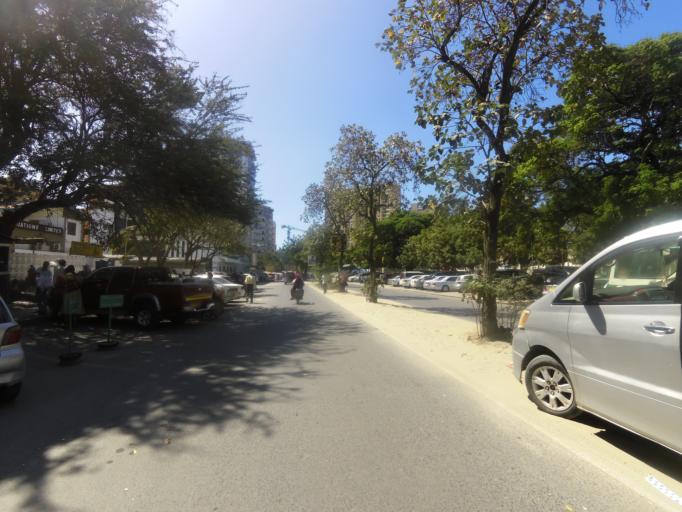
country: TZ
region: Dar es Salaam
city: Dar es Salaam
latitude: -6.8167
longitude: 39.2783
